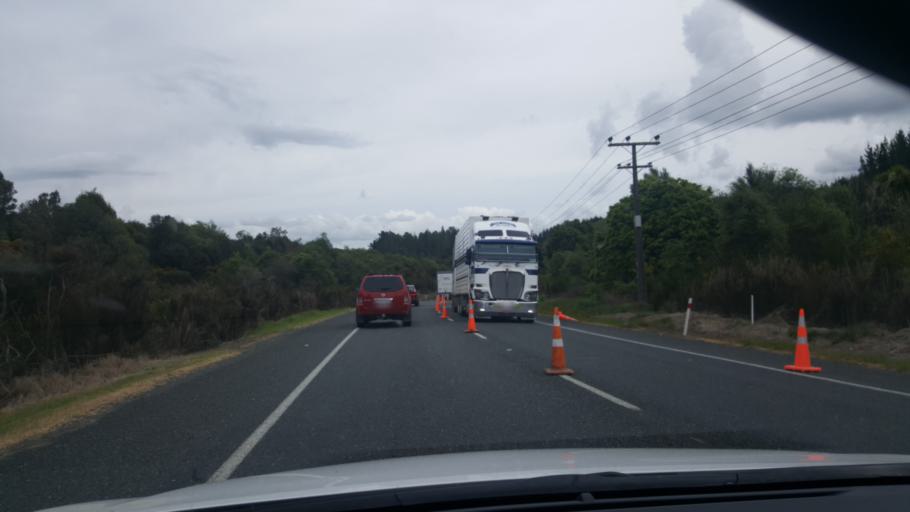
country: NZ
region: Bay of Plenty
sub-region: Rotorua District
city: Rotorua
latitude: -38.3196
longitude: 176.3739
